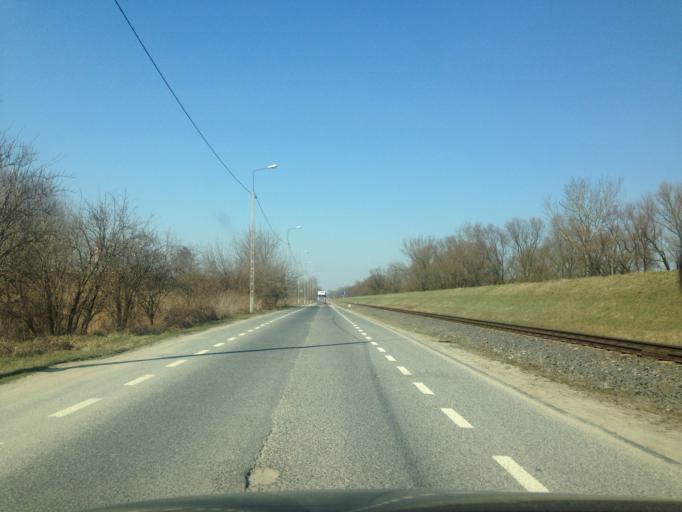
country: PL
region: Masovian Voivodeship
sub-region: Warszawa
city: Wilanow
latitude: 52.1717
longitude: 21.1214
